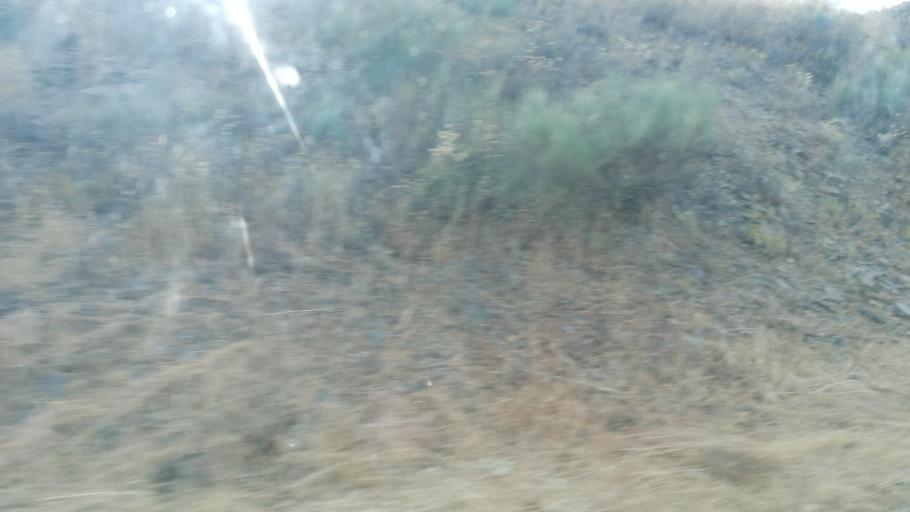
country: PT
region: Viseu
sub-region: Sao Joao da Pesqueira
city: Sao Joao da Pesqueira
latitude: 41.1156
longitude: -7.3863
